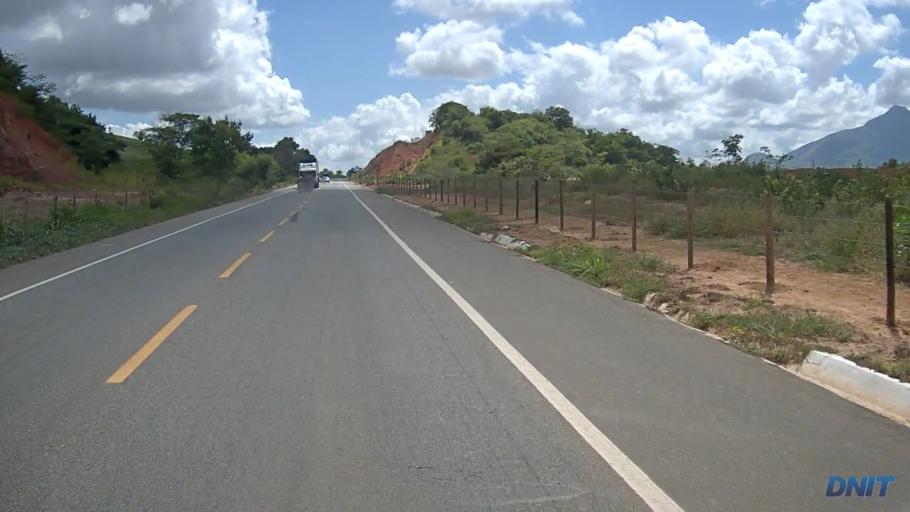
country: BR
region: Minas Gerais
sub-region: Governador Valadares
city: Governador Valadares
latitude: -18.9103
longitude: -42.0071
